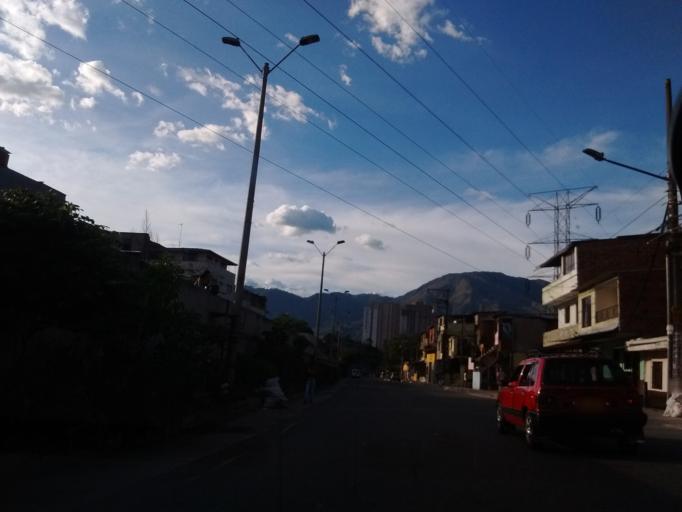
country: CO
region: Antioquia
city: Bello
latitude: 6.3056
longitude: -75.5580
